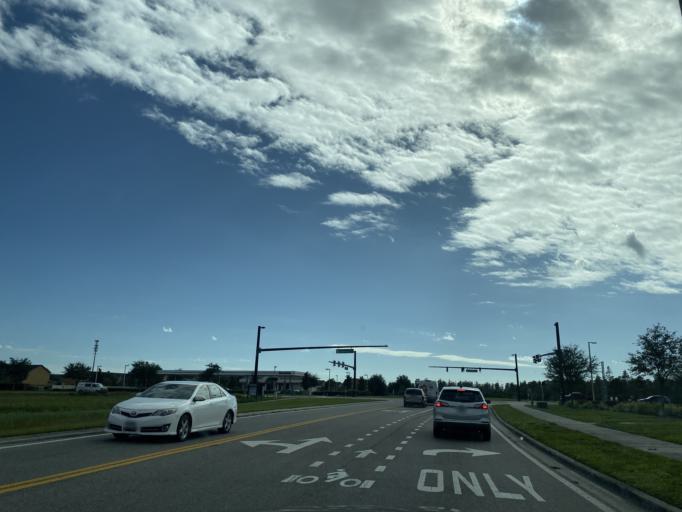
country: US
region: Florida
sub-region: Orange County
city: Azalea Park
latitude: 28.4794
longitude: -81.2471
